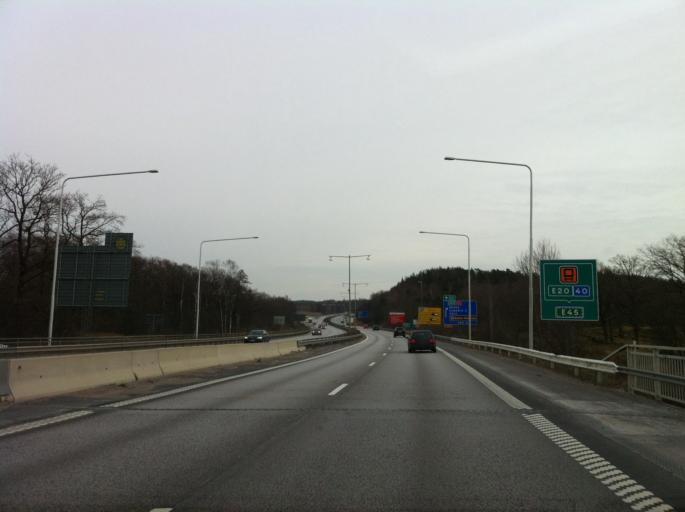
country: SE
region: Vaestra Goetaland
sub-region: Kungalvs Kommun
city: Kode
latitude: 57.9027
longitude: 11.9140
